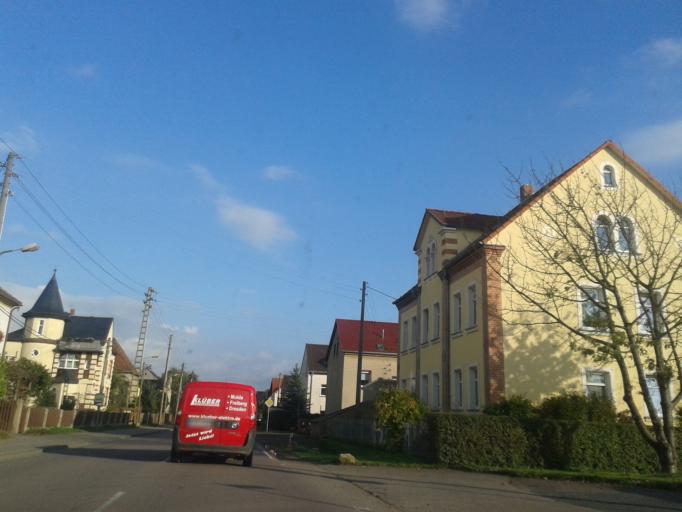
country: DE
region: Saxony
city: Nossen
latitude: 51.0540
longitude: 13.3476
